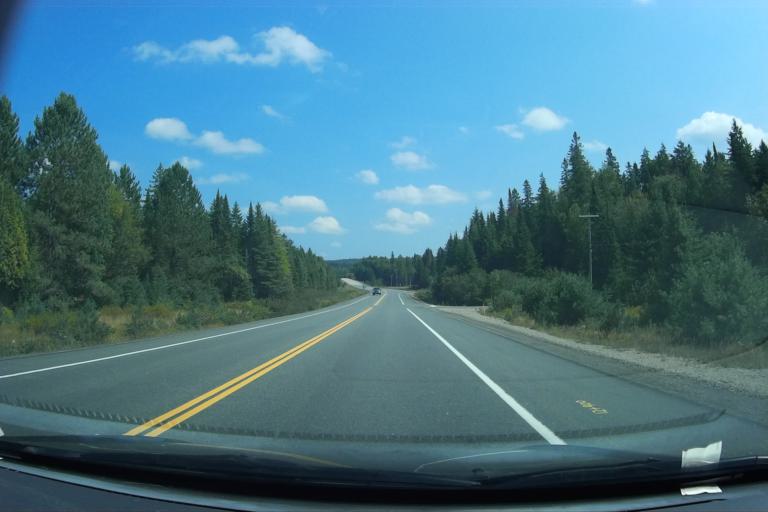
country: CA
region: Ontario
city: Huntsville
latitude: 45.5534
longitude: -78.5983
